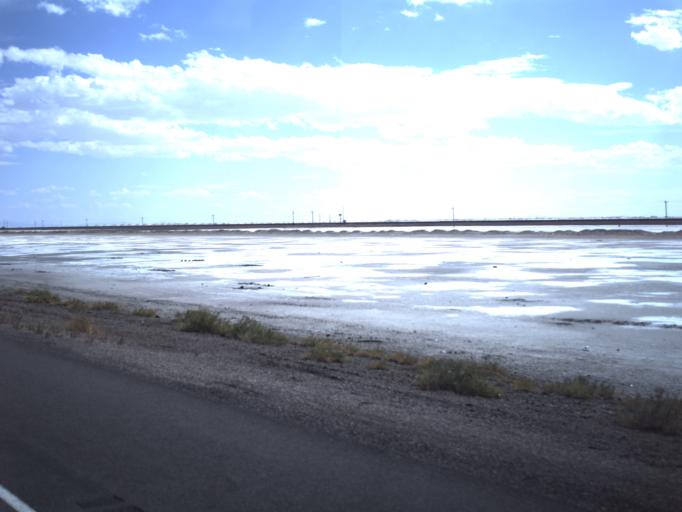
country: US
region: Utah
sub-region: Tooele County
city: Wendover
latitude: 40.7397
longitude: -113.9137
